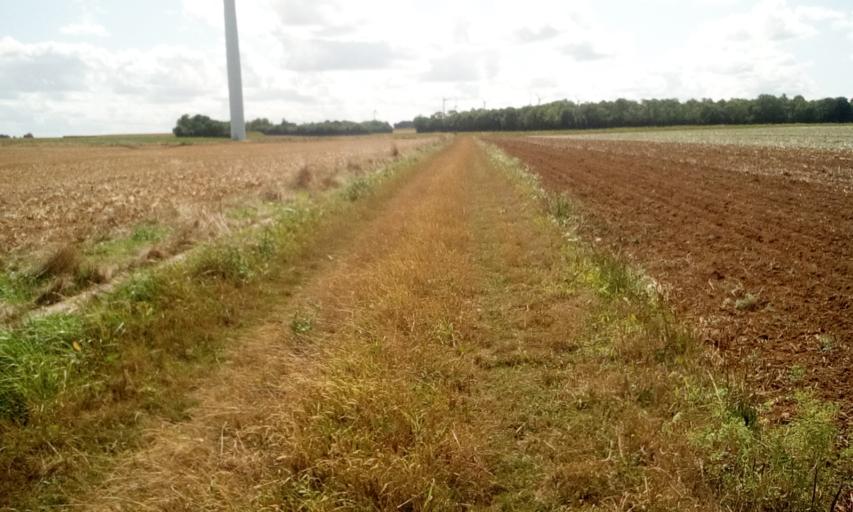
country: FR
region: Lower Normandy
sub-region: Departement du Calvados
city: Bellengreville
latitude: 49.1089
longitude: -0.2399
